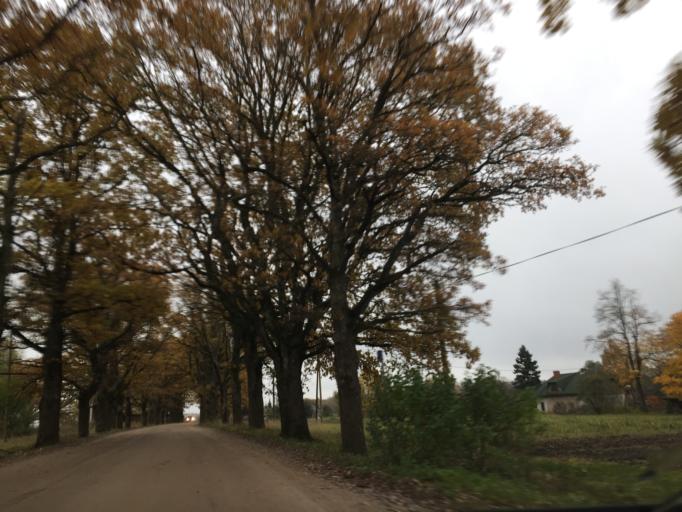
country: LV
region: Sigulda
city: Sigulda
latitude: 57.2661
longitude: 24.8710
